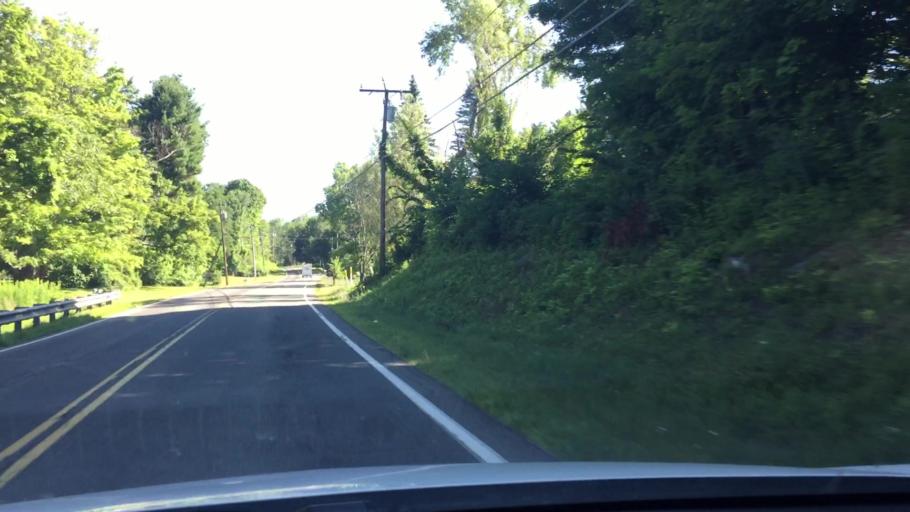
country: US
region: Massachusetts
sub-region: Berkshire County
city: Lenox
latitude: 42.4091
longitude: -73.3145
